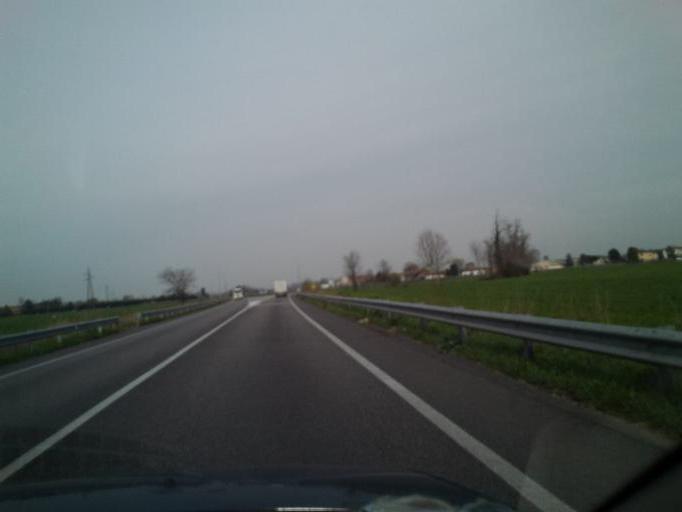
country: IT
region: Lombardy
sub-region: Provincia di Mantova
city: Marmirolo
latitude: 45.2173
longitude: 10.7474
